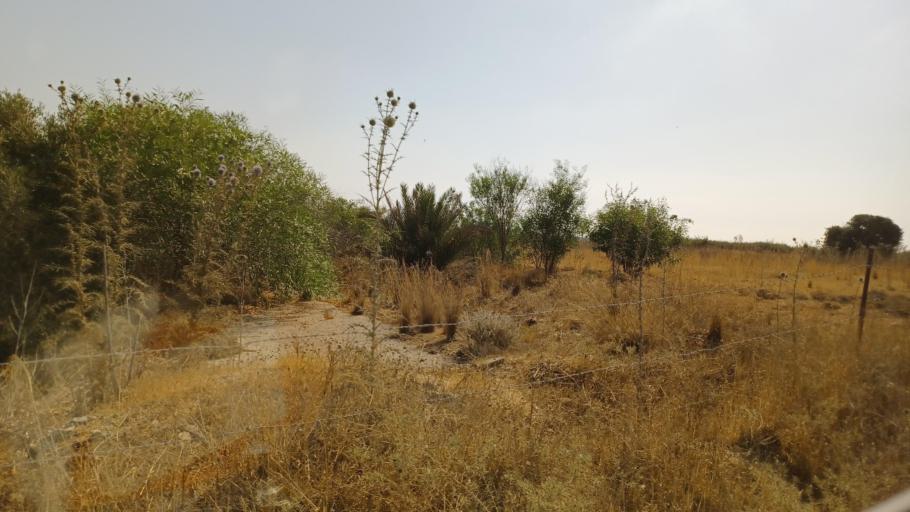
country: CY
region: Ammochostos
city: Deryneia
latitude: 35.0694
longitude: 33.9704
